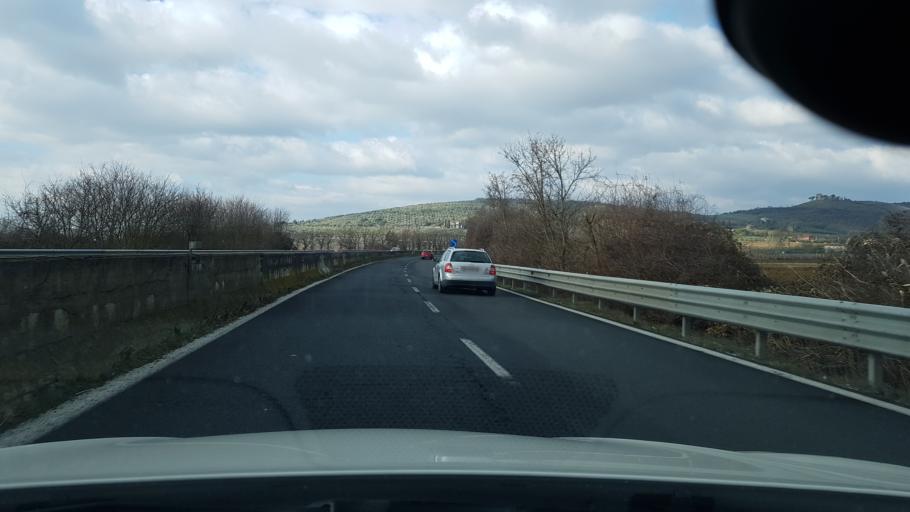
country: IT
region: Umbria
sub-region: Provincia di Perugia
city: Tuoro sul Trasimeno
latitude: 43.1954
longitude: 12.0669
